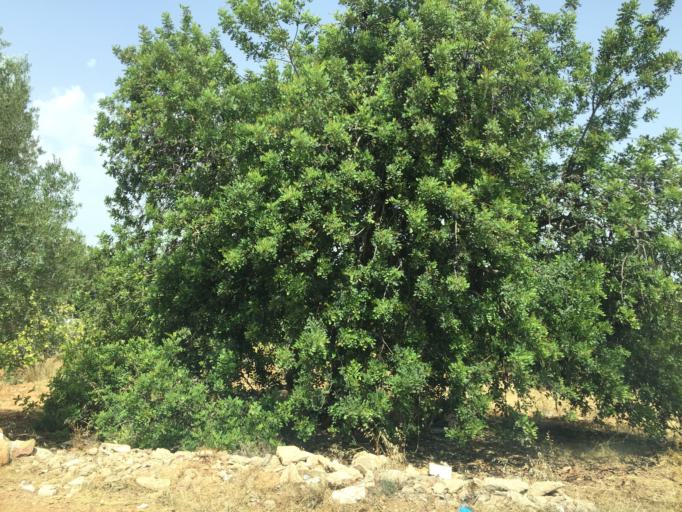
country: PT
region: Faro
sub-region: Loule
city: Boliqueime
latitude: 37.1287
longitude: -8.1483
